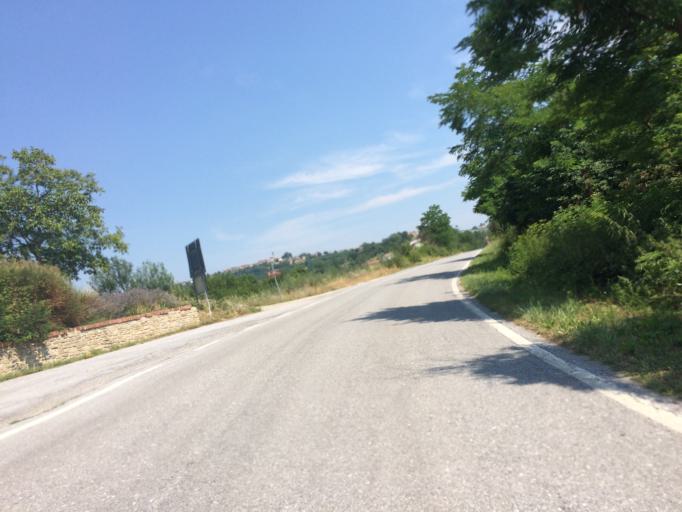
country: IT
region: Piedmont
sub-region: Provincia di Cuneo
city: Cissone
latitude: 44.5617
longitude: 8.0353
